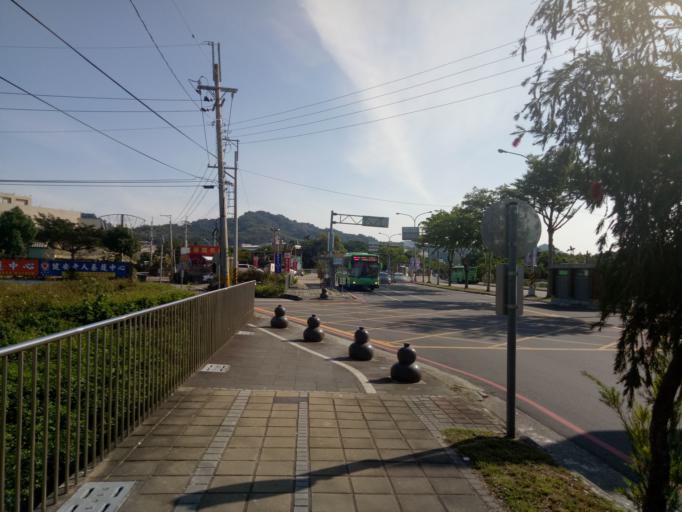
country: TW
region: Taiwan
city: Fengyuan
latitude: 24.2602
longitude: 120.7364
